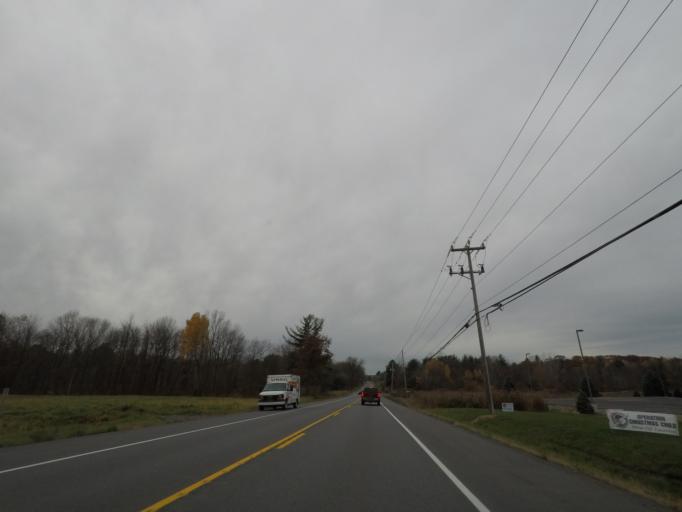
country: US
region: New York
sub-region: Saratoga County
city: Mechanicville
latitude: 42.8650
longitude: -73.7423
